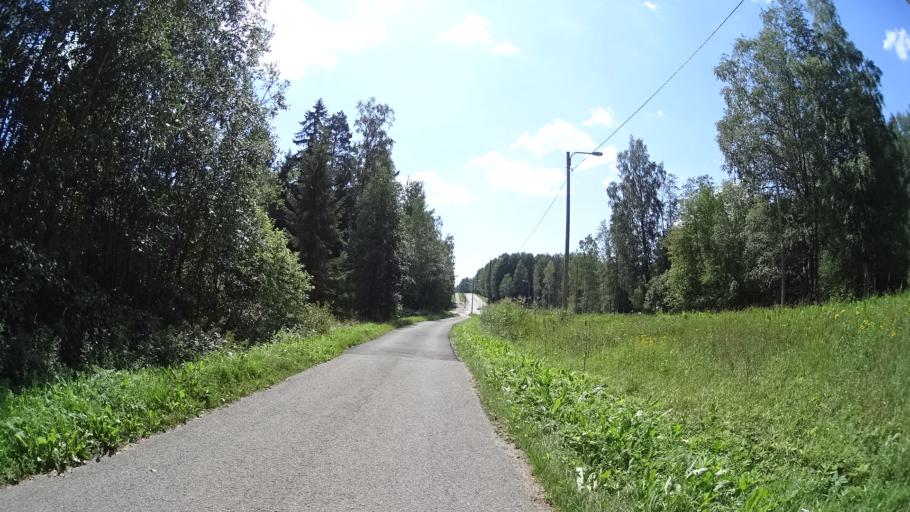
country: FI
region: Uusimaa
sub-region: Helsinki
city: Vantaa
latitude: 60.3306
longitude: 25.0034
